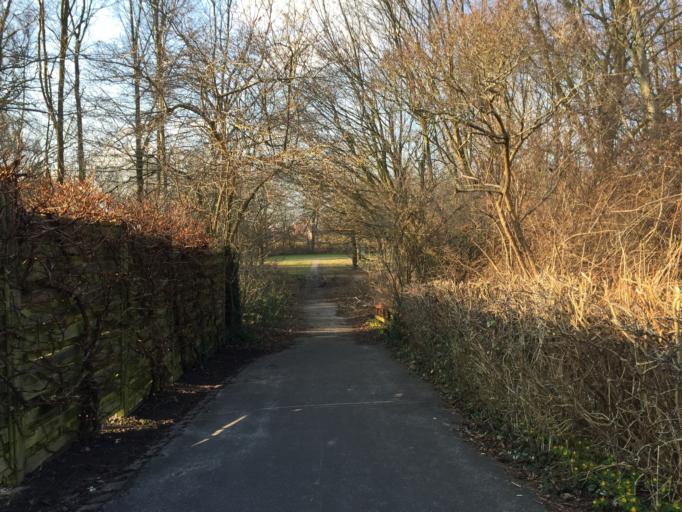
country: DK
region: South Denmark
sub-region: Odense Kommune
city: Odense
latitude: 55.3871
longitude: 10.4107
